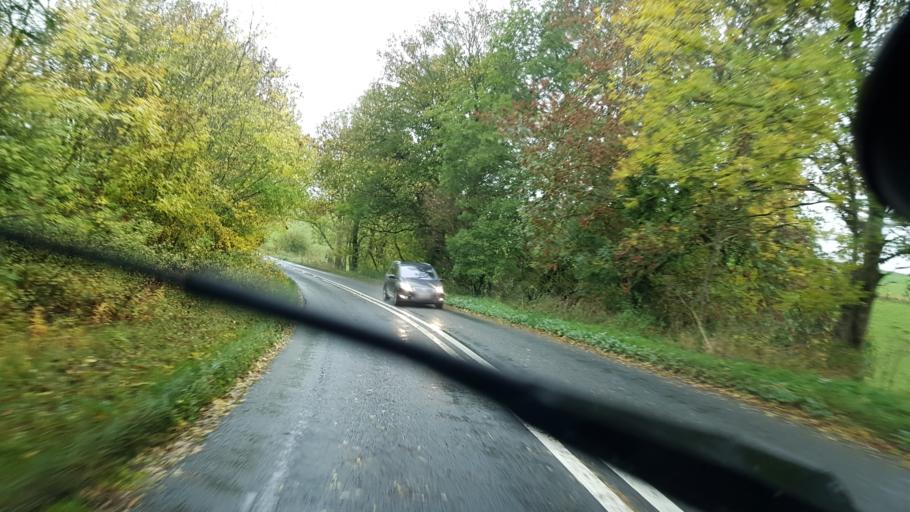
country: GB
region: England
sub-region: Gloucestershire
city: Stow on the Wold
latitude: 51.9423
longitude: -1.7502
